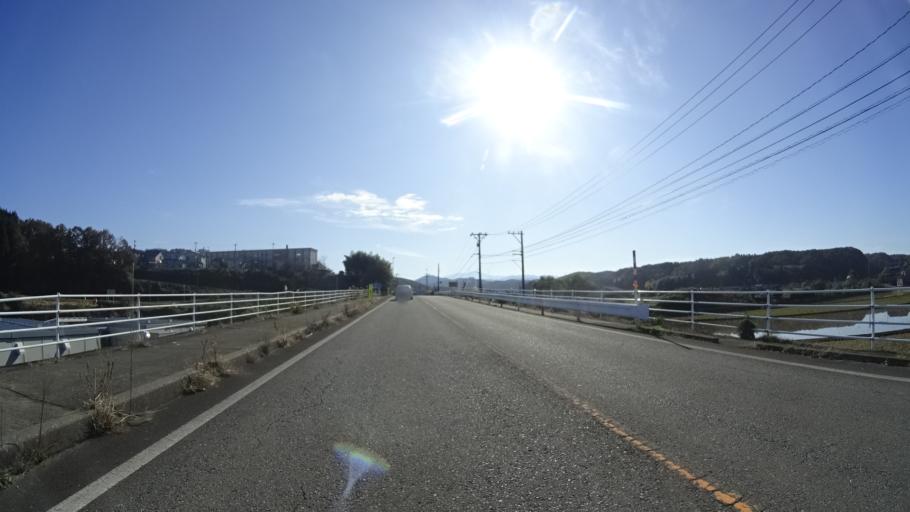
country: JP
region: Ishikawa
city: Komatsu
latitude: 36.3983
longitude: 136.5158
